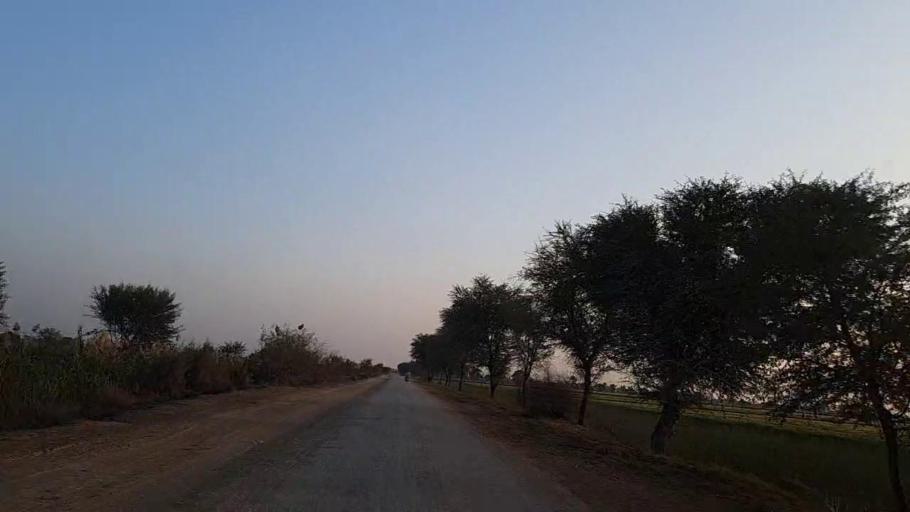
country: PK
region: Sindh
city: Shahdadpur
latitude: 25.9315
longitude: 68.5052
